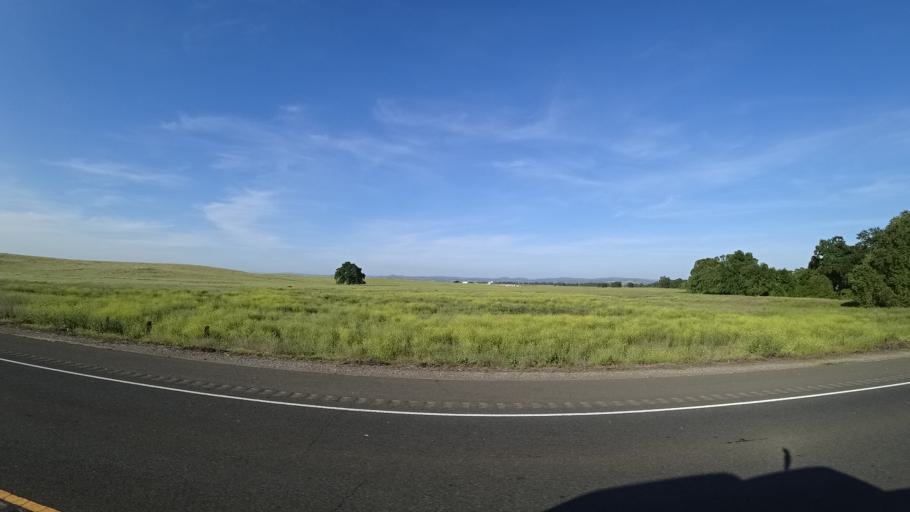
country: US
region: California
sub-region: Placer County
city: Sheridan
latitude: 38.9385
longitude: -121.3517
